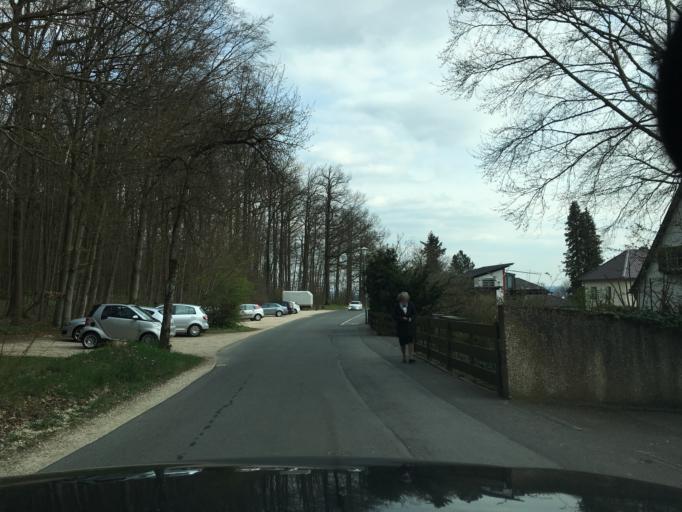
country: DE
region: Bavaria
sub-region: Upper Palatinate
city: Amberg
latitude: 49.4519
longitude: 11.8773
